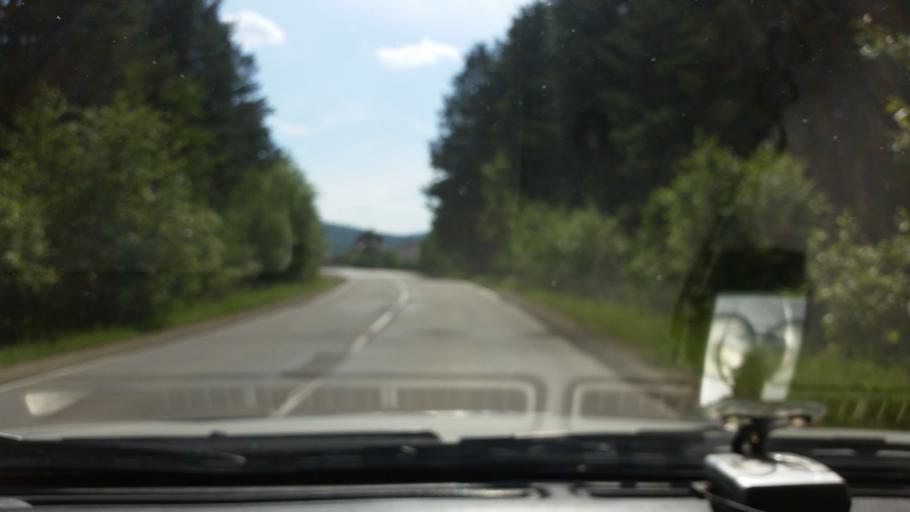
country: RU
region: Irkutsk
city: Baklashi
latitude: 52.2073
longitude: 103.9604
